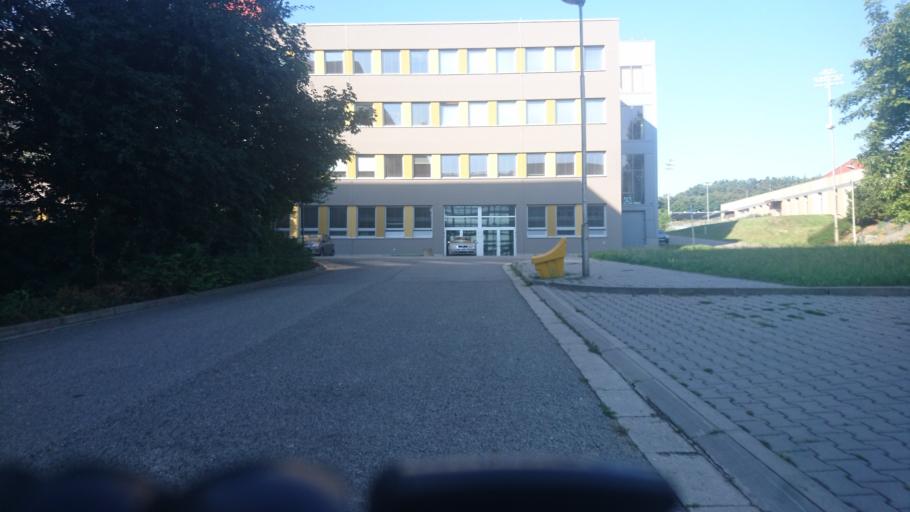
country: CZ
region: South Moravian
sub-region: Mesto Brno
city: Mokra Hora
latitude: 49.2254
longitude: 16.5754
